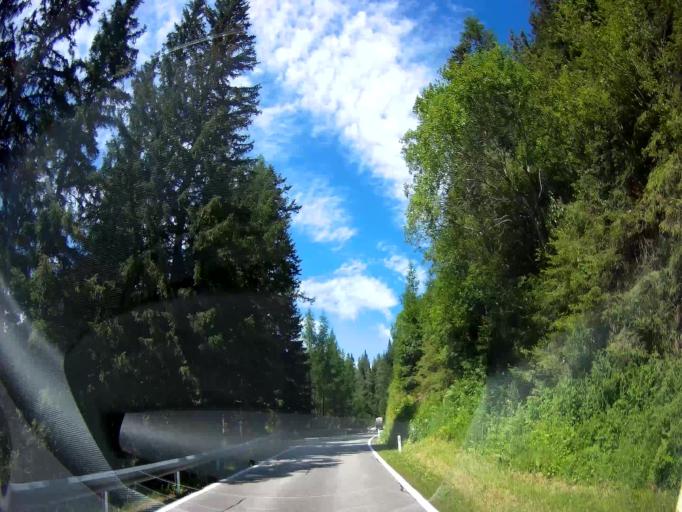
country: AT
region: Carinthia
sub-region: Politischer Bezirk Sankt Veit an der Glan
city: Glodnitz
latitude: 46.9341
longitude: 14.0534
